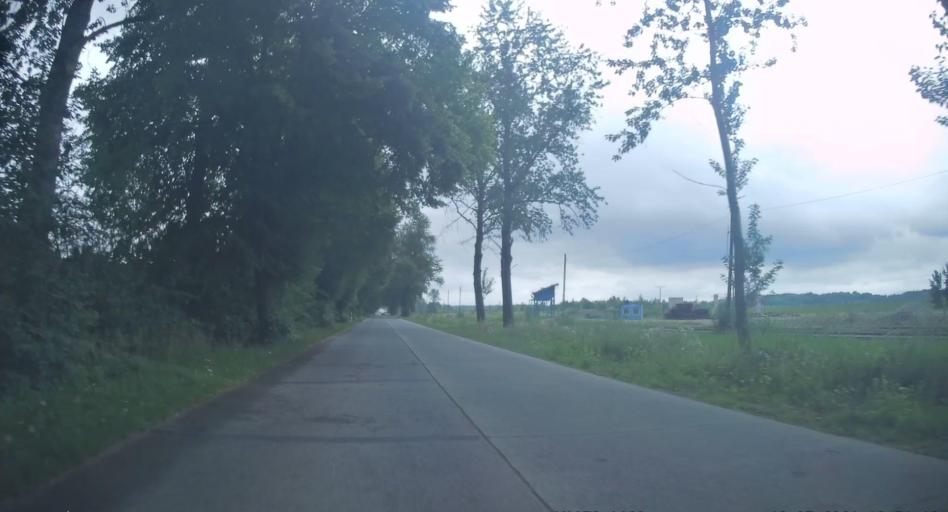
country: PL
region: Opole Voivodeship
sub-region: Powiat nyski
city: Paczkow
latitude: 50.4820
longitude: 16.9924
